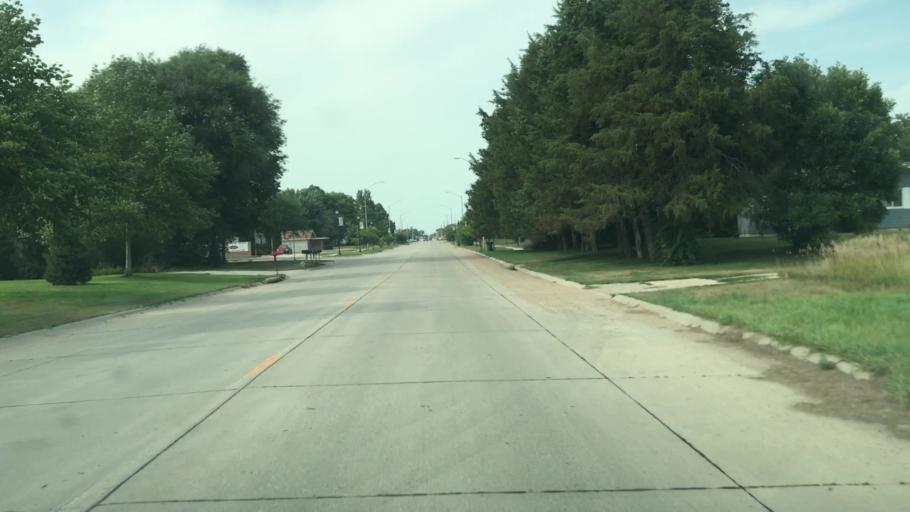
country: US
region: Nebraska
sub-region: Hall County
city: Wood River
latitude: 40.9961
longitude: -98.6075
